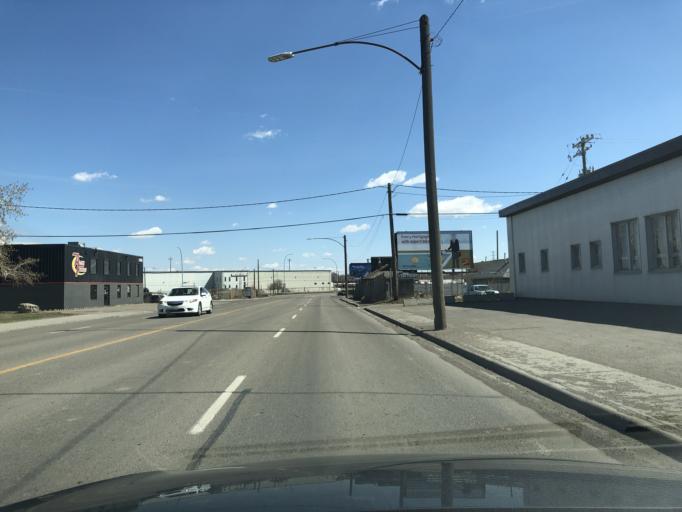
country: CA
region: Alberta
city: Calgary
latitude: 51.0186
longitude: -114.0220
